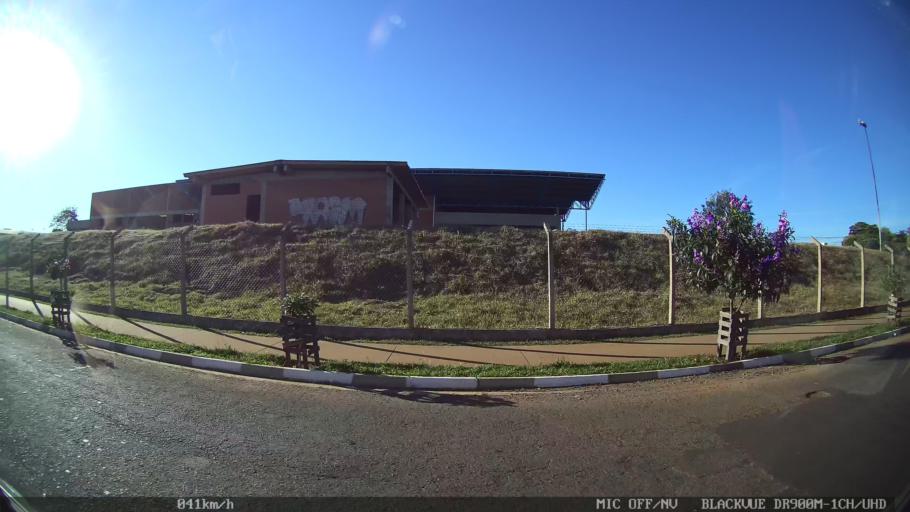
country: BR
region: Sao Paulo
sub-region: Franca
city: Franca
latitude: -20.5676
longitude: -47.4046
